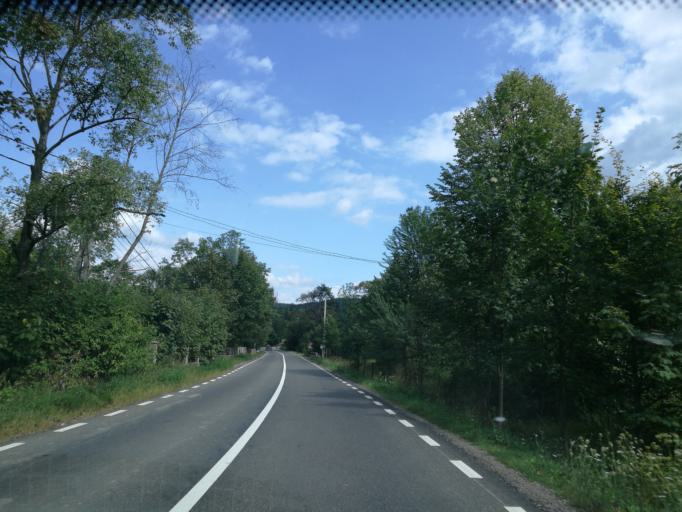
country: RO
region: Suceava
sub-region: Comuna Sucevita
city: Sucevita
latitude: 47.7594
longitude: 25.6786
